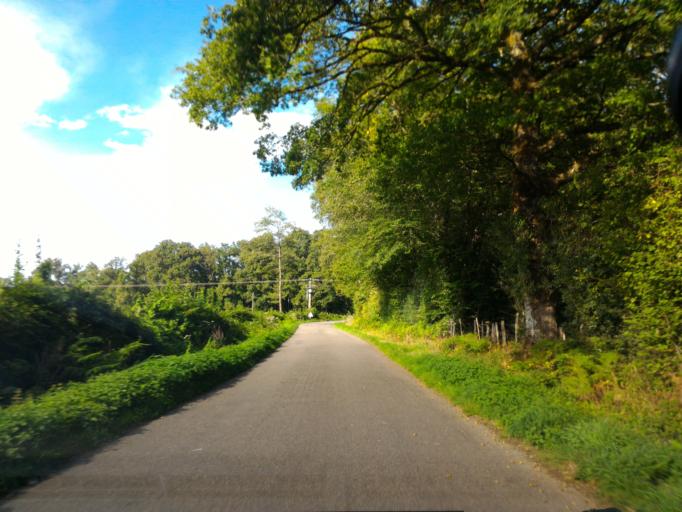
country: FR
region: Poitou-Charentes
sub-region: Departement de la Charente
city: Brigueuil
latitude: 45.9847
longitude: 0.8249
